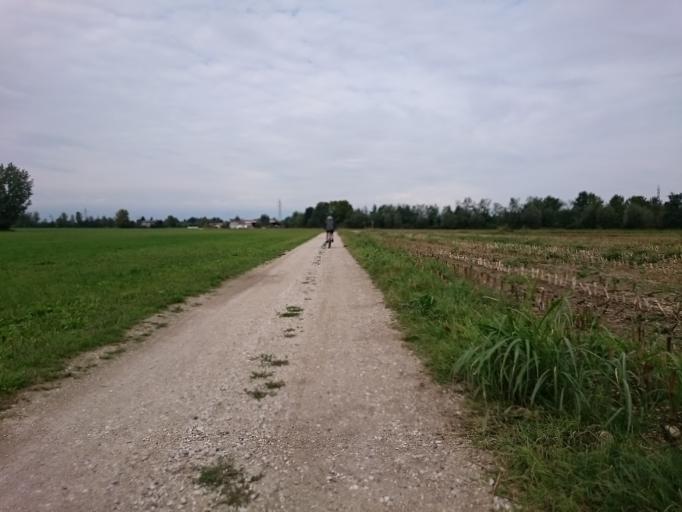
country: IT
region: Veneto
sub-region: Provincia di Vicenza
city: Quinto Vicentino
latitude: 45.5669
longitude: 11.6657
